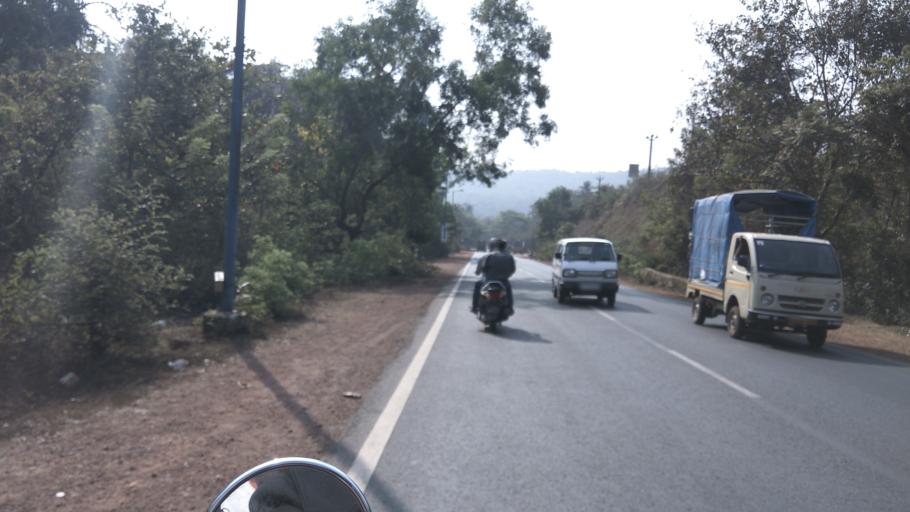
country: IN
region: Goa
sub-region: North Goa
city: Bandora
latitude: 15.4442
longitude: 73.9746
